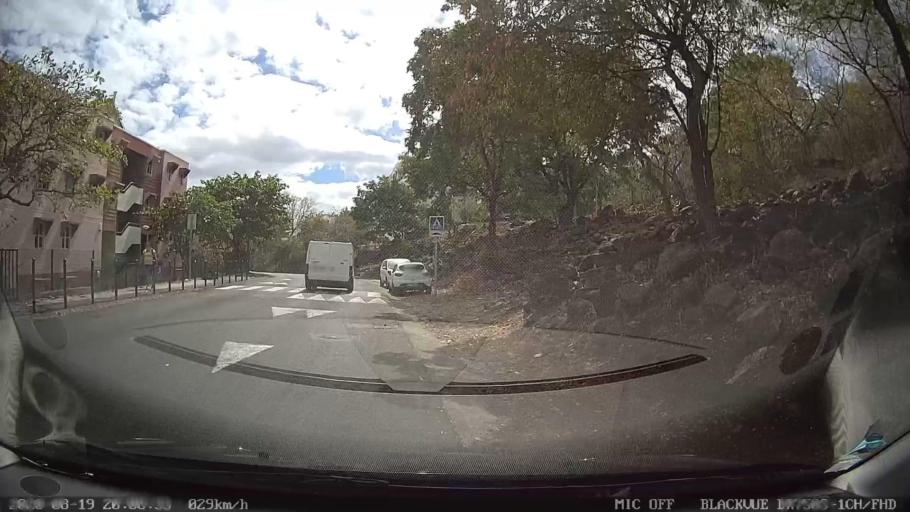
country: RE
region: Reunion
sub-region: Reunion
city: La Possession
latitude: -20.9527
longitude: 55.3321
